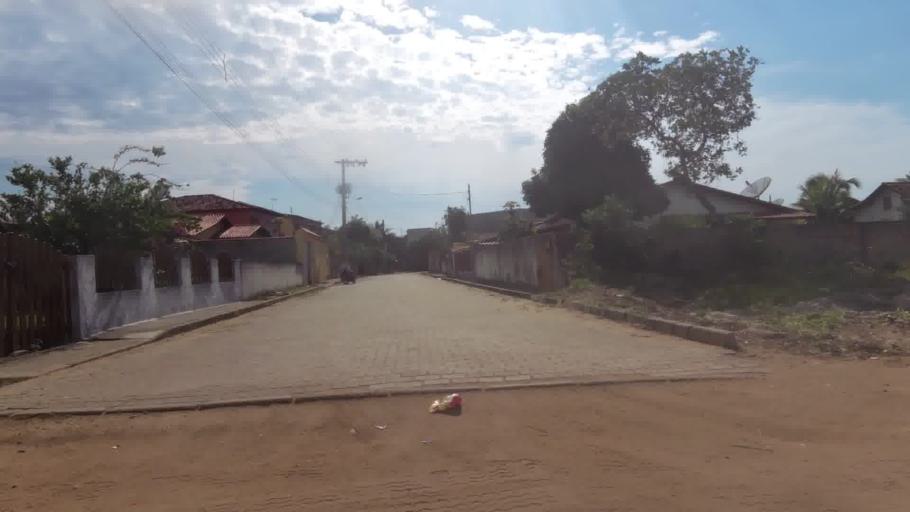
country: BR
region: Espirito Santo
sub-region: Piuma
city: Piuma
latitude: -20.8487
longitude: -40.7517
